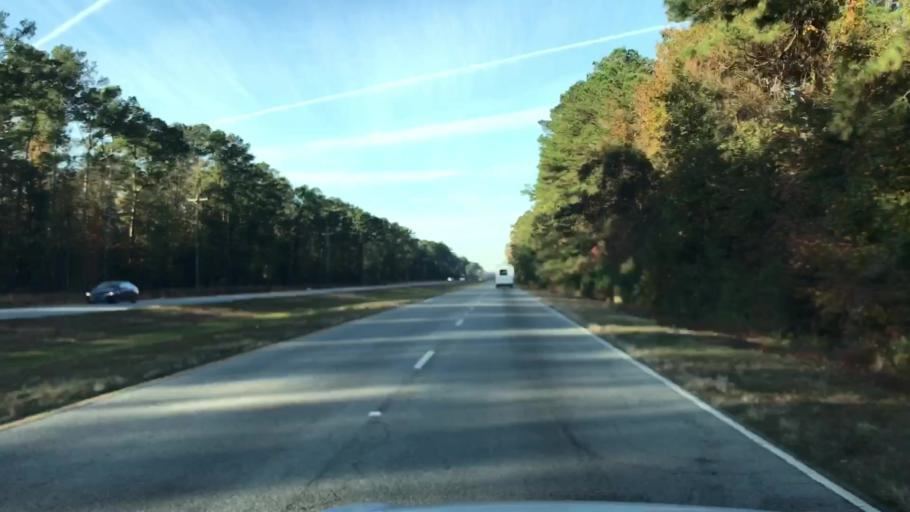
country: US
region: South Carolina
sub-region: Charleston County
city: Ravenel
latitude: 32.7637
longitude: -80.3035
